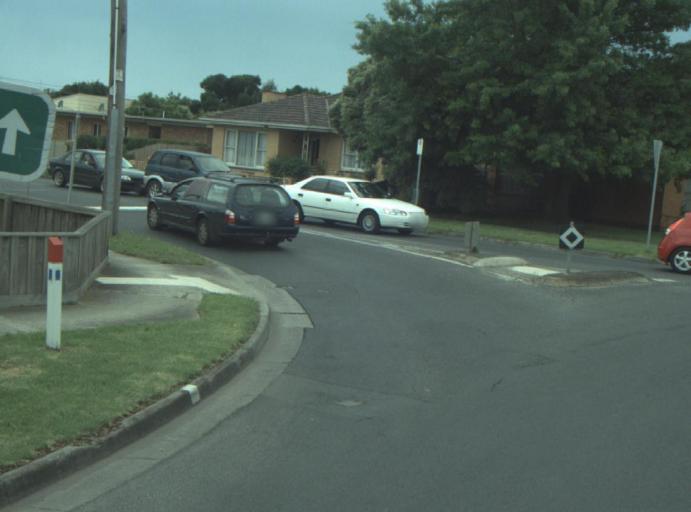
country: AU
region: Victoria
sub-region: Greater Geelong
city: Breakwater
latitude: -38.1801
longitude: 144.3825
